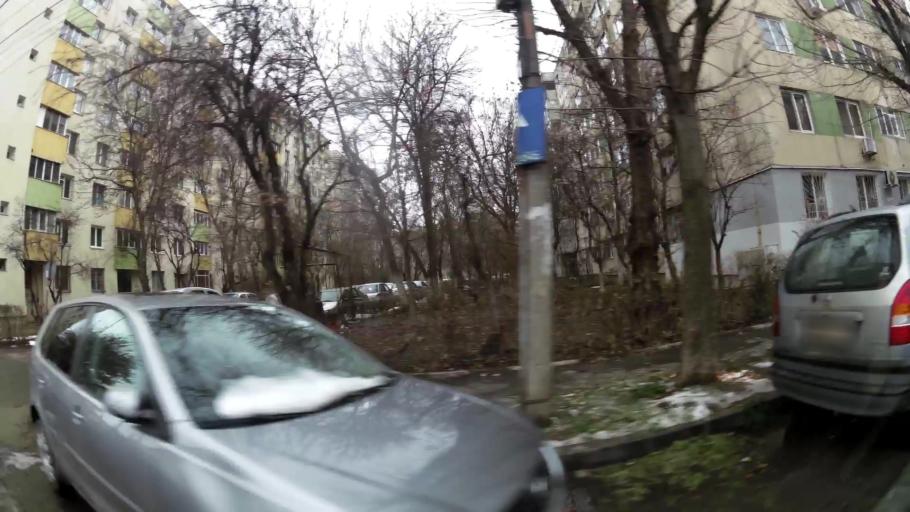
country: RO
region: Bucuresti
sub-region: Municipiul Bucuresti
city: Bucharest
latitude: 44.4612
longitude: 26.1246
